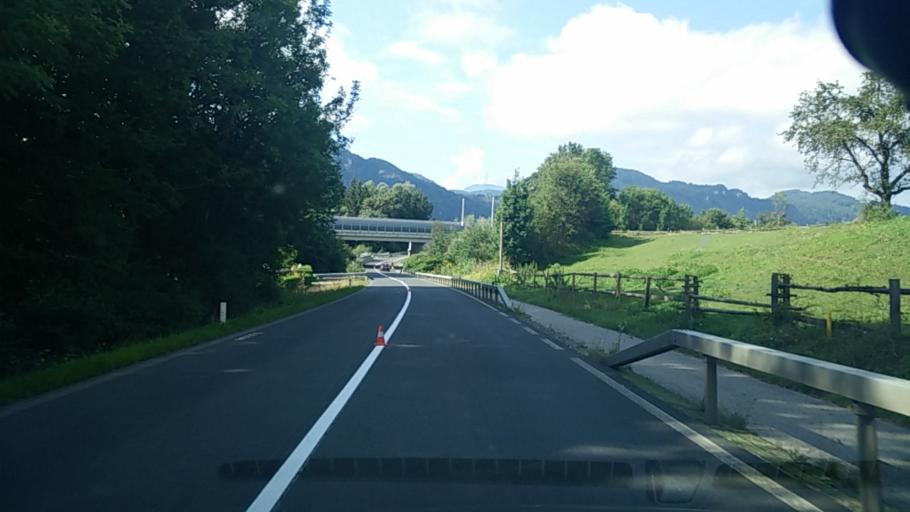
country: AT
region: Carinthia
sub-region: Politischer Bezirk Klagenfurt Land
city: Grafenstein
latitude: 46.6149
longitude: 14.5039
